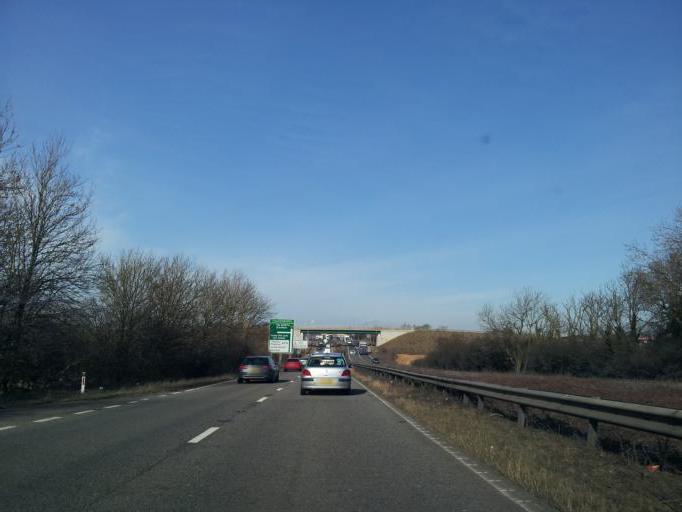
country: GB
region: England
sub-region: District of Rutland
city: Clipsham
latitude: 52.7989
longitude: -0.6107
